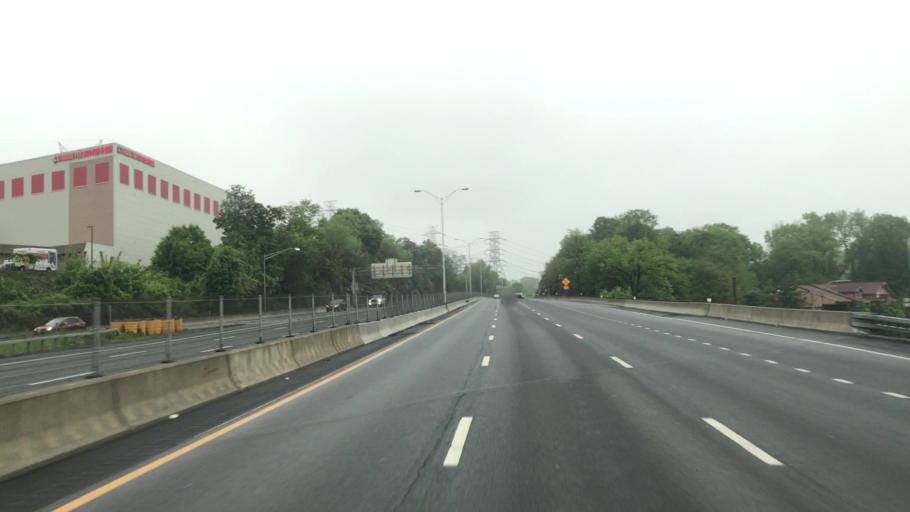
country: US
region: New York
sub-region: Westchester County
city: Bronxville
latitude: 40.9384
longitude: -73.8555
